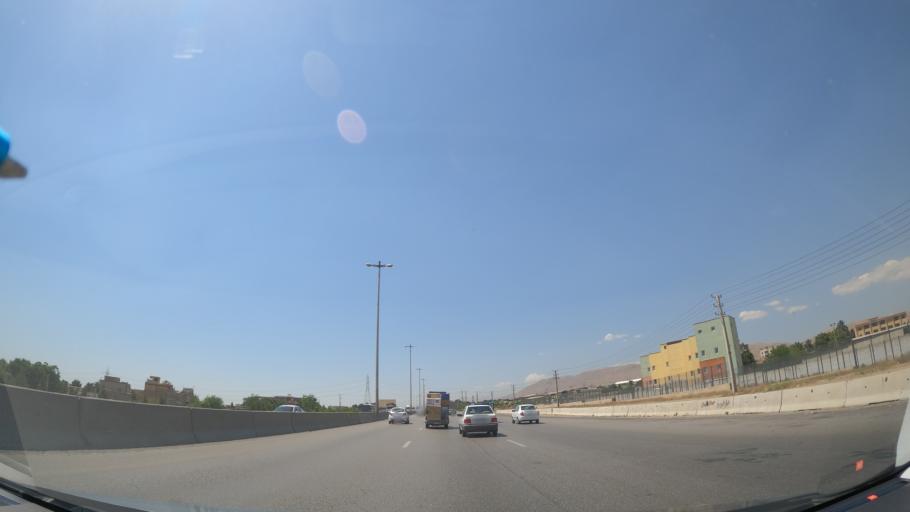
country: IR
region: Alborz
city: Karaj
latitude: 35.8677
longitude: 50.9007
